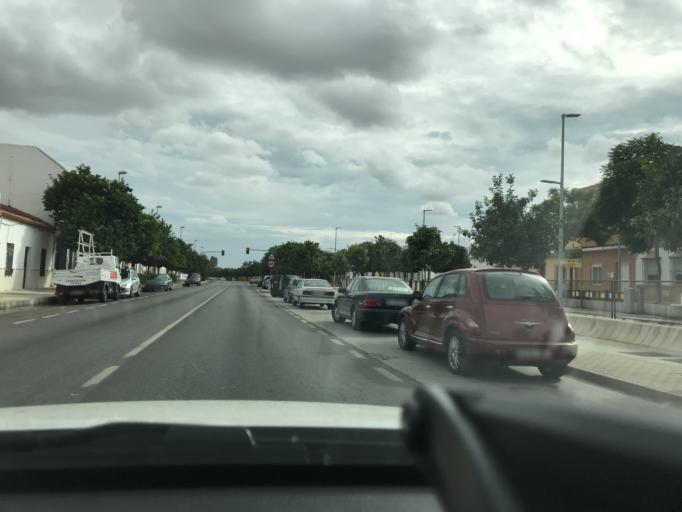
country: ES
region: Andalusia
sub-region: Provincia de Sevilla
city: La Rinconada
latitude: 37.4849
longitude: -5.9786
